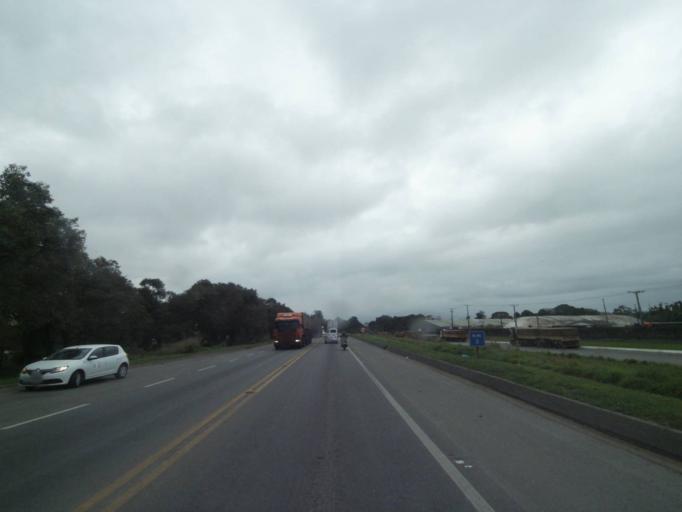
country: BR
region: Parana
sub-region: Paranagua
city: Paranagua
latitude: -25.5343
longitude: -48.5533
